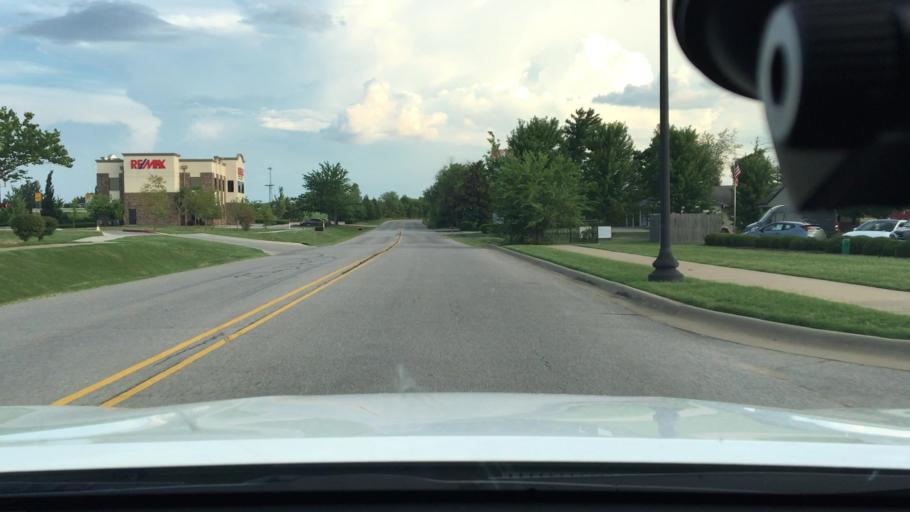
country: US
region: Arkansas
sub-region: Benton County
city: Bentonville
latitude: 36.3390
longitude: -94.1839
